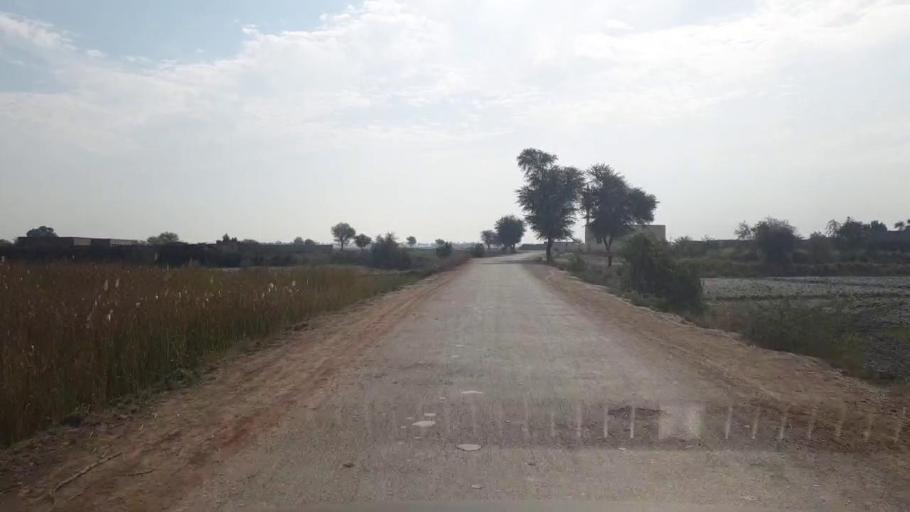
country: PK
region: Sindh
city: Hala
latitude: 26.0010
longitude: 68.4055
